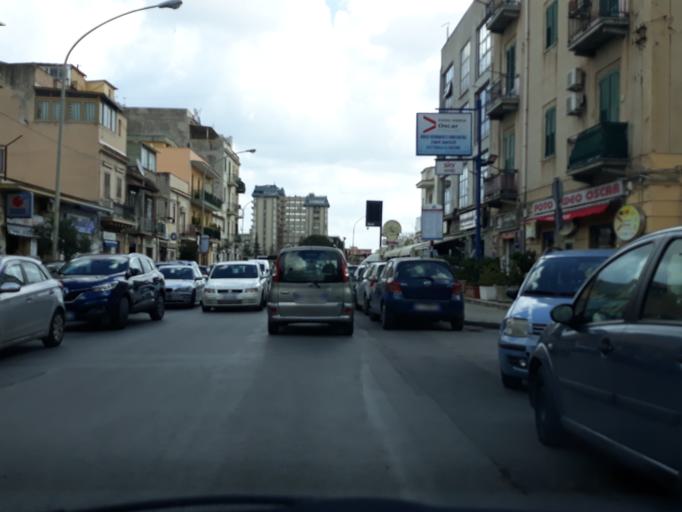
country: IT
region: Sicily
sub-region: Palermo
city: Palermo
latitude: 38.1259
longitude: 13.3133
